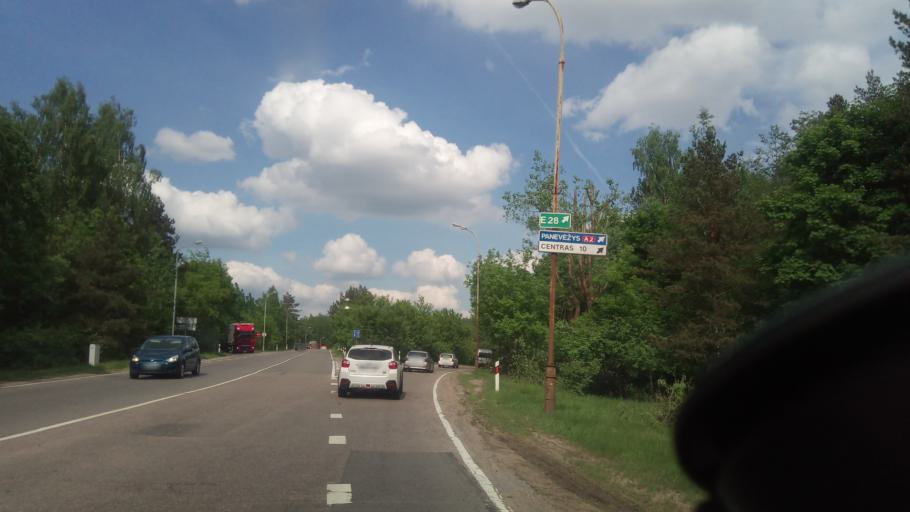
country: LT
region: Vilnius County
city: Lazdynai
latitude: 54.6382
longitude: 25.1796
